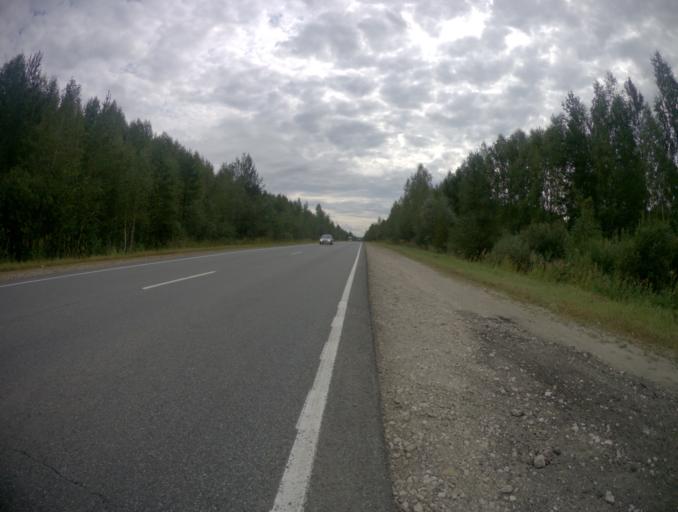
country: RU
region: Vladimir
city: Golovino
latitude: 55.9614
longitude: 40.5587
